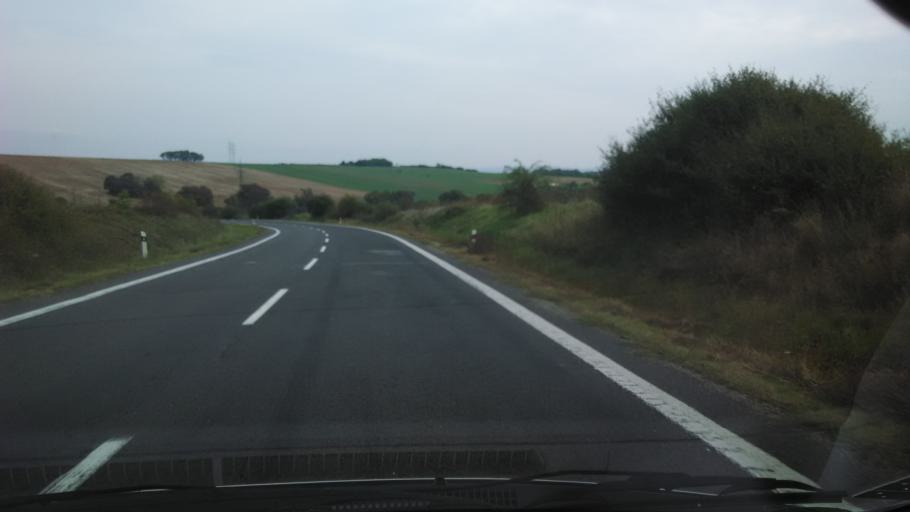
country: SK
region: Nitriansky
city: Zeliezovce
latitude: 48.1216
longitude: 18.7467
